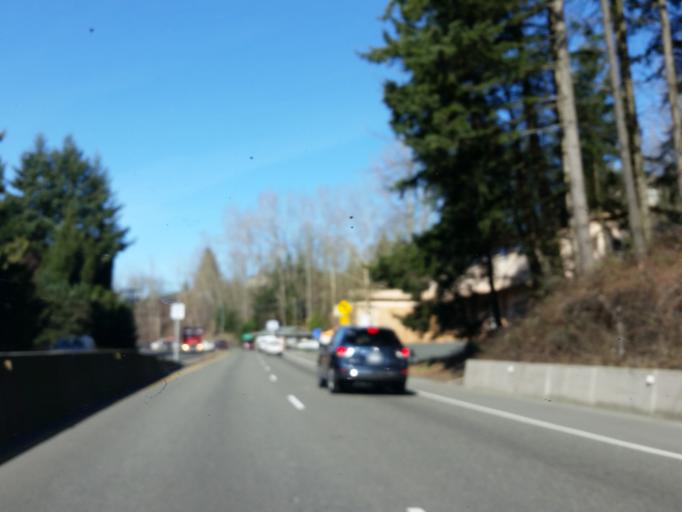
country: US
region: Washington
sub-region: King County
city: Bothell
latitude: 47.7576
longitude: -122.1975
